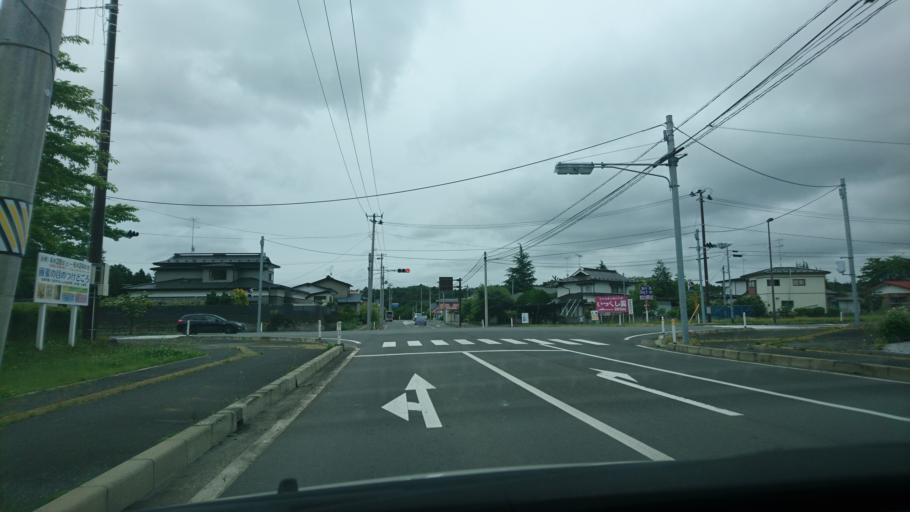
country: JP
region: Iwate
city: Ichinoseki
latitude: 38.9467
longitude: 141.0503
